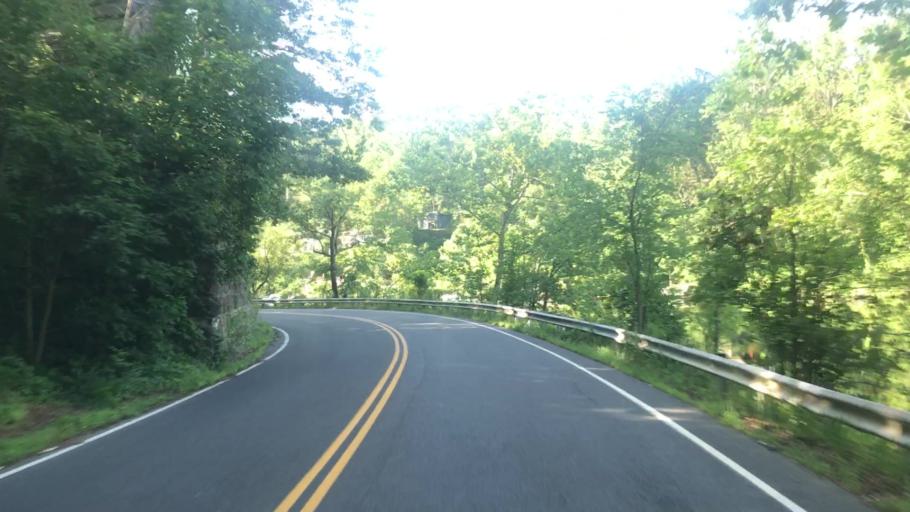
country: US
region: Connecticut
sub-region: Fairfield County
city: Newtown
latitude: 41.4358
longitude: -73.2639
